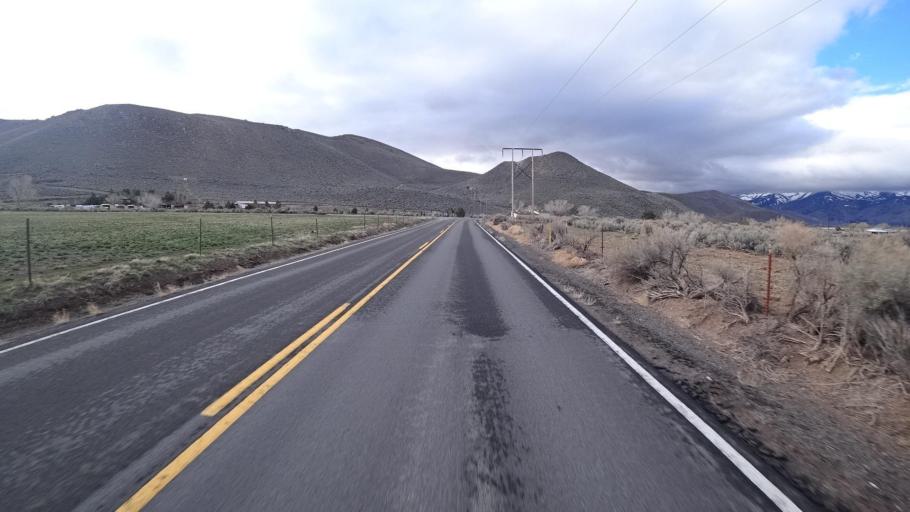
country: US
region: Nevada
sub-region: Carson City
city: Carson City
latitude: 39.2480
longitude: -119.7567
